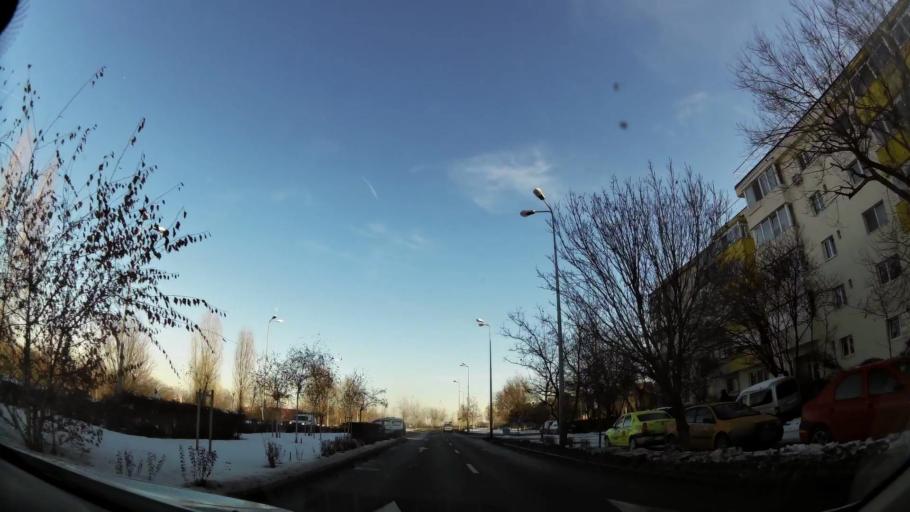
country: RO
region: Ilfov
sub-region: Comuna Fundeni-Dobroesti
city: Fundeni
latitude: 44.4555
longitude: 26.1454
